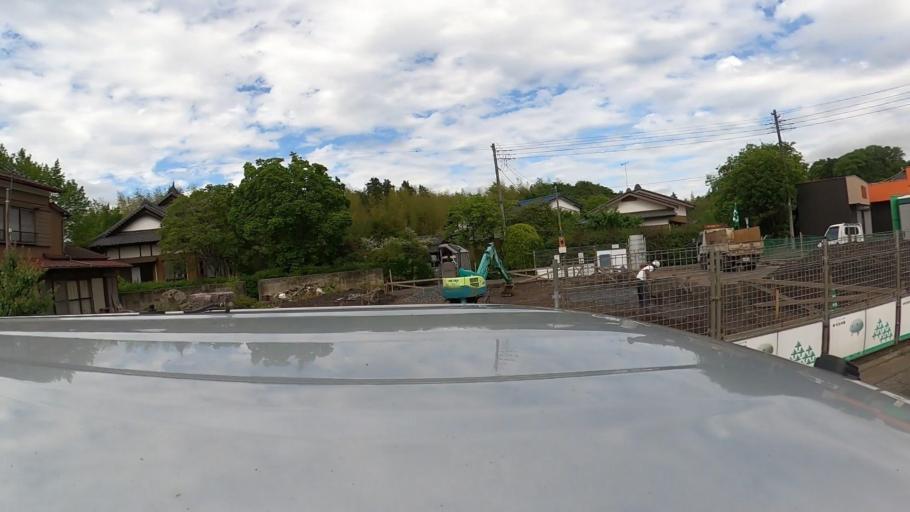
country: JP
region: Ibaraki
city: Ushiku
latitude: 35.9779
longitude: 140.1749
